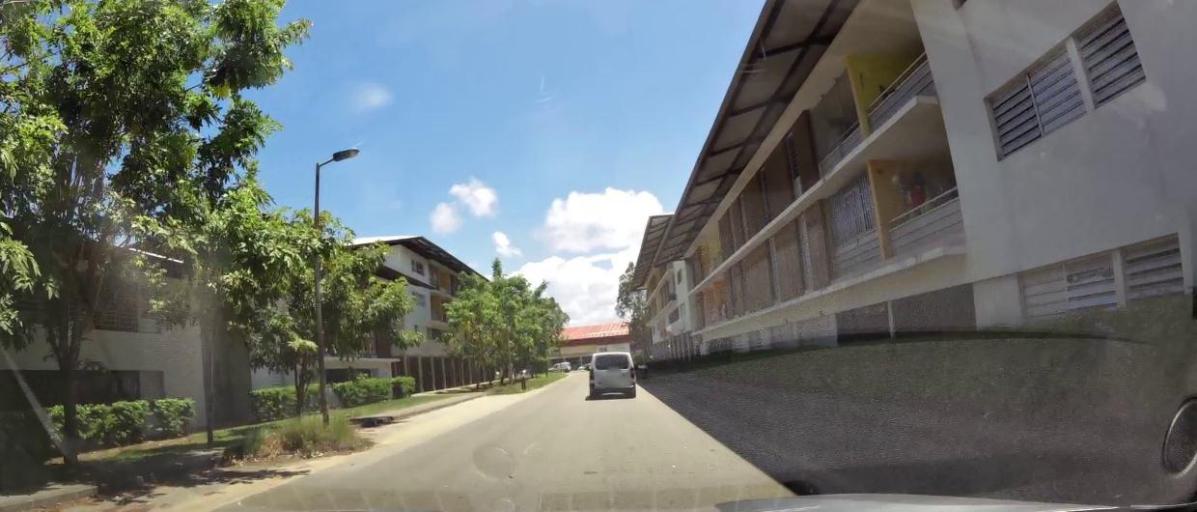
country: GF
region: Guyane
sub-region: Guyane
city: Kourou
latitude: 5.1607
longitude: -52.6424
